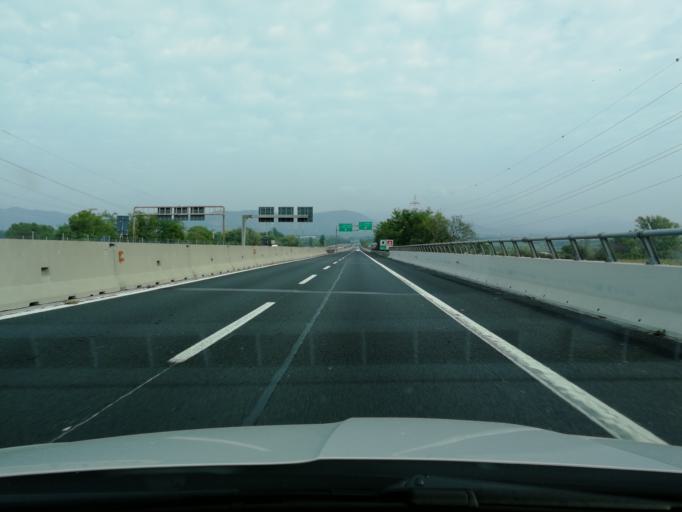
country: IT
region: Latium
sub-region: Citta metropolitana di Roma Capitale
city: Bagni di Tivoli
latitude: 41.9266
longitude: 12.7177
